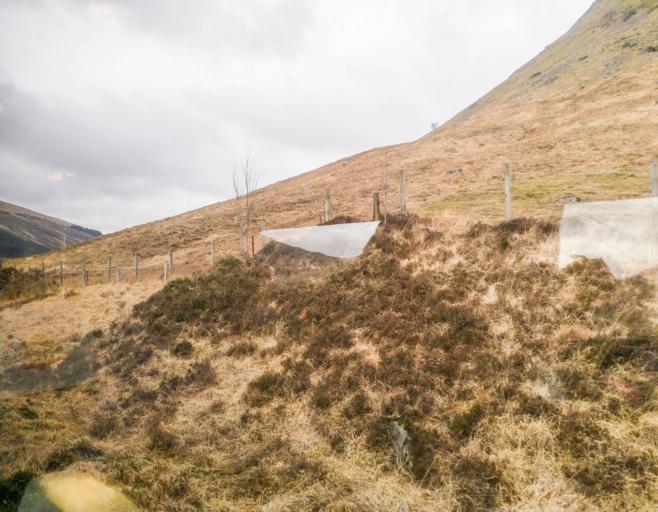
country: GB
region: Scotland
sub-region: Argyll and Bute
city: Garelochhead
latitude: 56.4876
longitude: -4.7152
